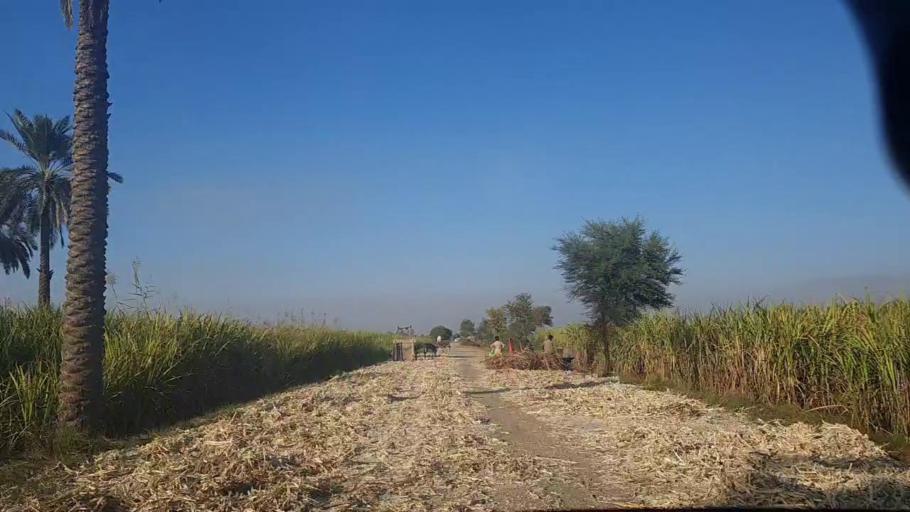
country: PK
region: Sindh
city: Sobhadero
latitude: 27.4110
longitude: 68.4225
